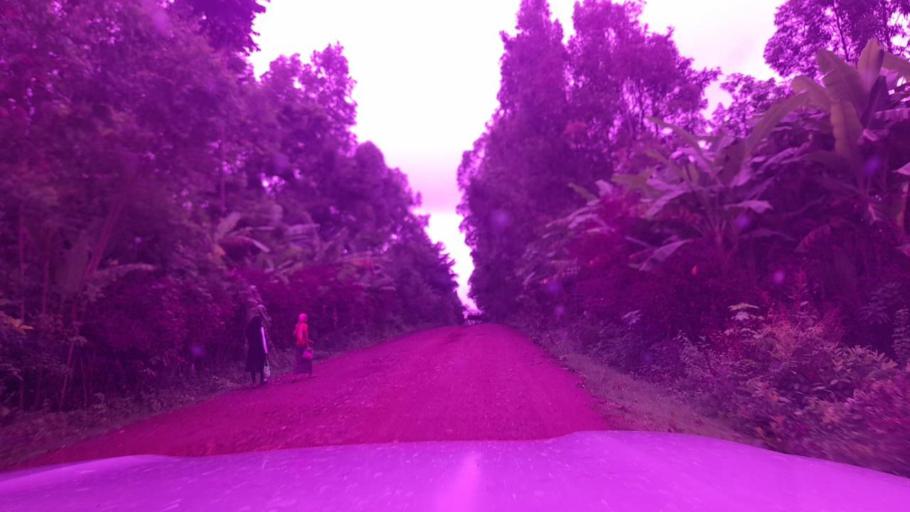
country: ET
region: Southern Nations, Nationalities, and People's Region
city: Bonga
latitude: 7.5826
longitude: 36.0199
